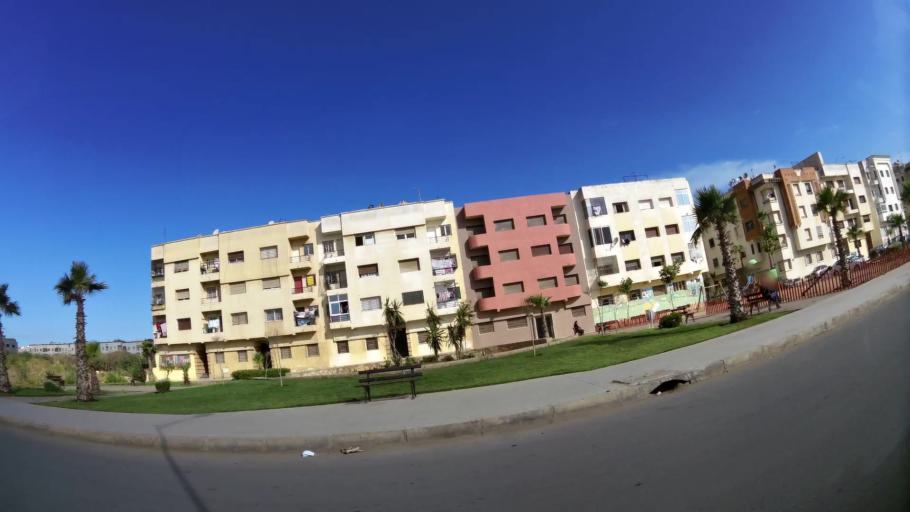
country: MA
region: Rabat-Sale-Zemmour-Zaer
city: Sale
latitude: 34.0603
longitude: -6.8060
